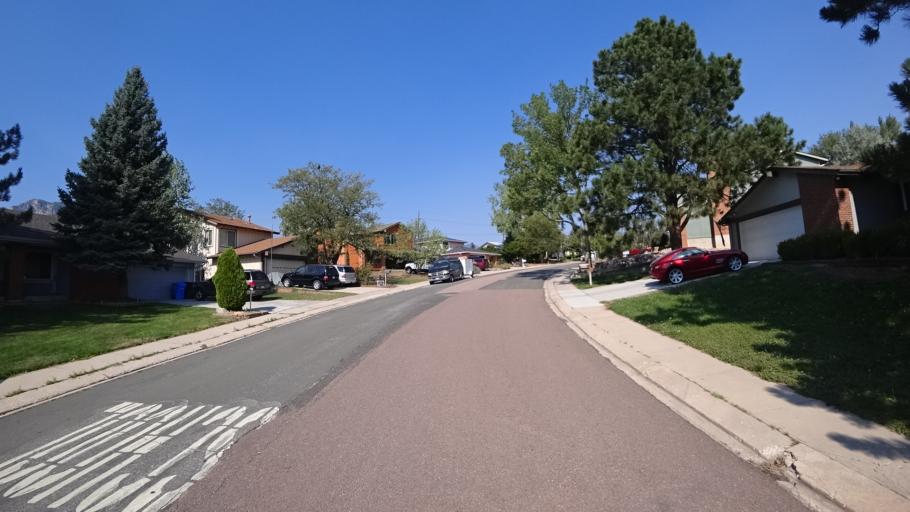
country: US
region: Colorado
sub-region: El Paso County
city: Stratmoor
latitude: 38.7851
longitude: -104.8196
